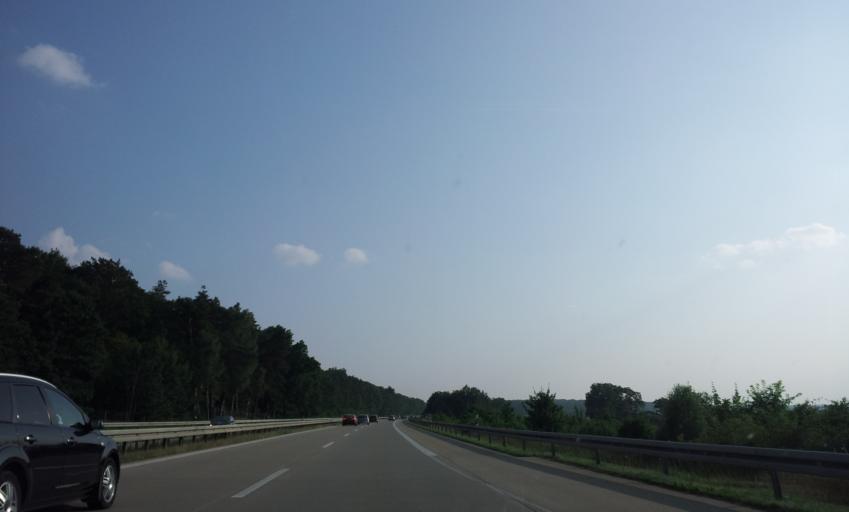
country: DE
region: Brandenburg
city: Gerswalde
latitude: 53.1259
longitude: 13.8778
